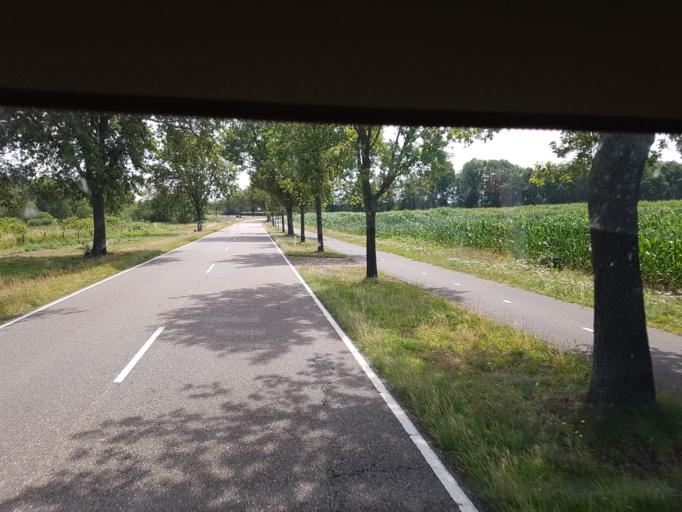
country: NL
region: Limburg
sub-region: Gemeente Nederweert
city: Nederweert
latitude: 51.2653
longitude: 5.7821
